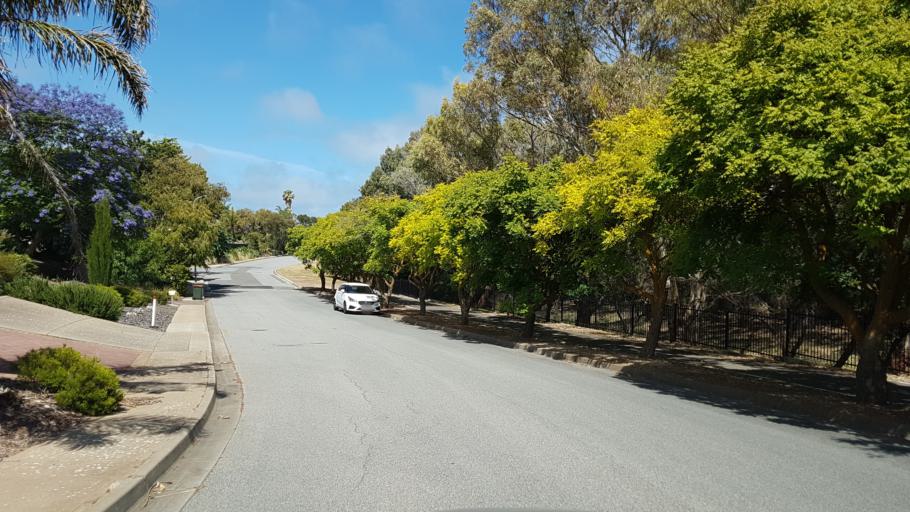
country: AU
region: South Australia
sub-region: Marion
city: Happy Valley
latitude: -35.0736
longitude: 138.5183
